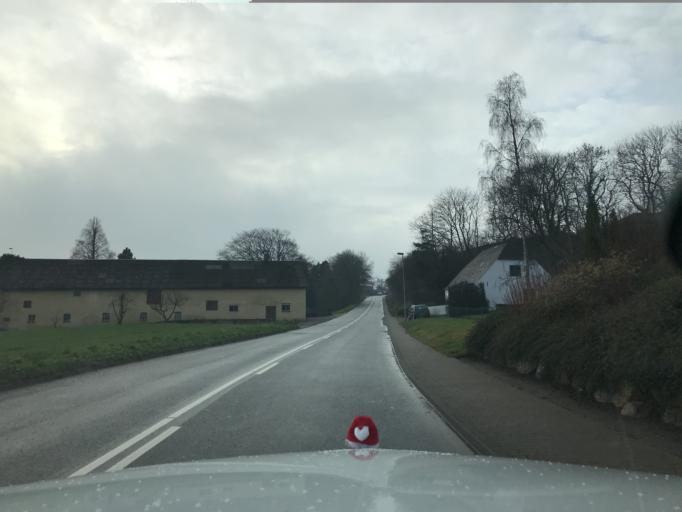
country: DK
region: South Denmark
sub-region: Sonderborg Kommune
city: Grasten
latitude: 54.8939
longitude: 9.5640
